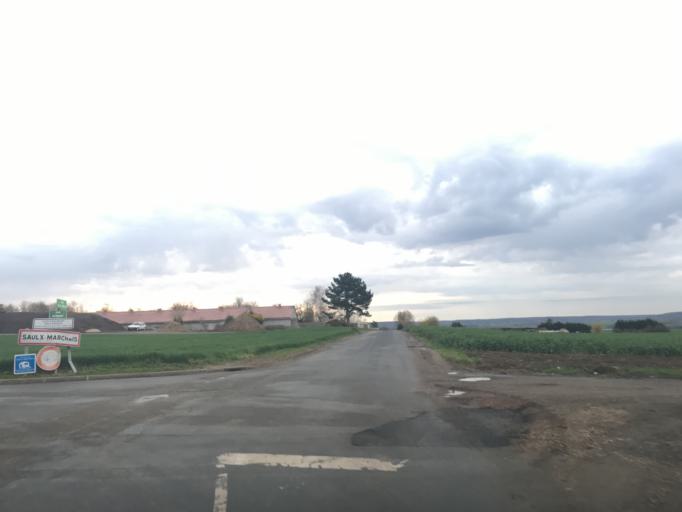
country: FR
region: Ile-de-France
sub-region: Departement des Yvelines
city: Beynes
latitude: 48.8339
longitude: 1.8324
